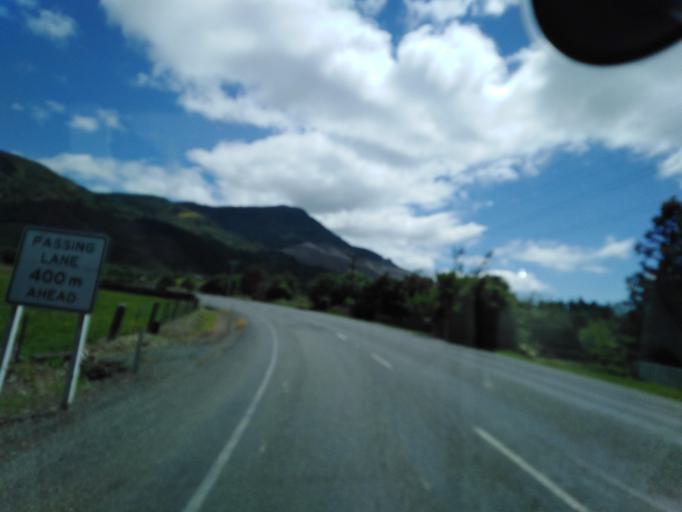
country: NZ
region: Nelson
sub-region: Nelson City
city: Nelson
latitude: -41.2134
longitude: 173.3959
